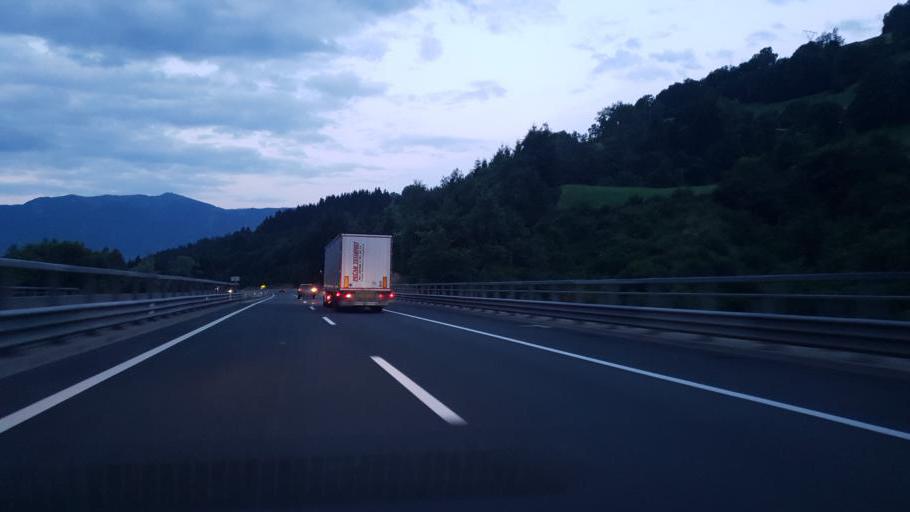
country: AT
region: Carinthia
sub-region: Politischer Bezirk Spittal an der Drau
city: Trebesing
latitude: 46.8576
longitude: 13.5010
